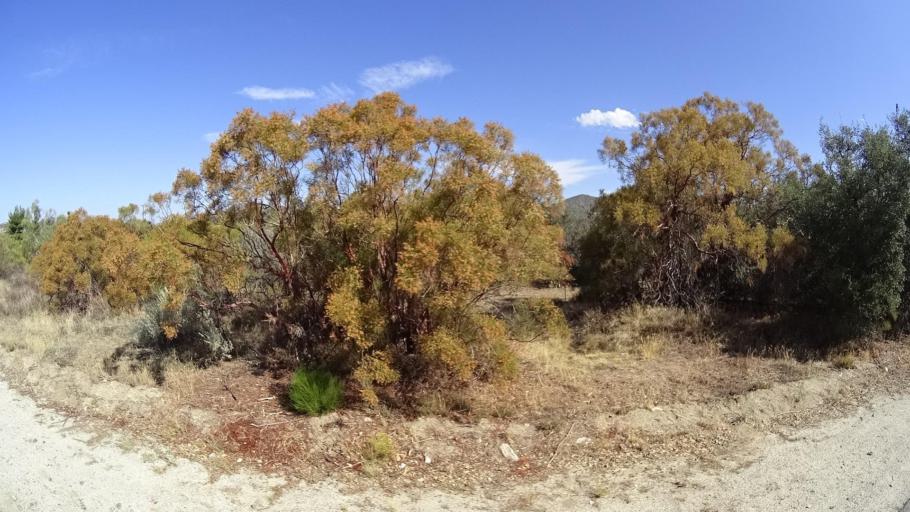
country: US
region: California
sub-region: Riverside County
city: Anza
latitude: 33.3846
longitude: -116.6814
